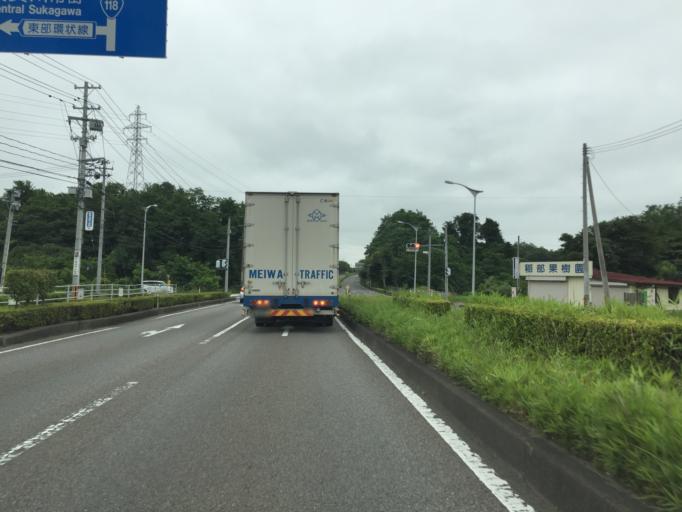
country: JP
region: Fukushima
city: Sukagawa
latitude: 37.2726
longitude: 140.3695
